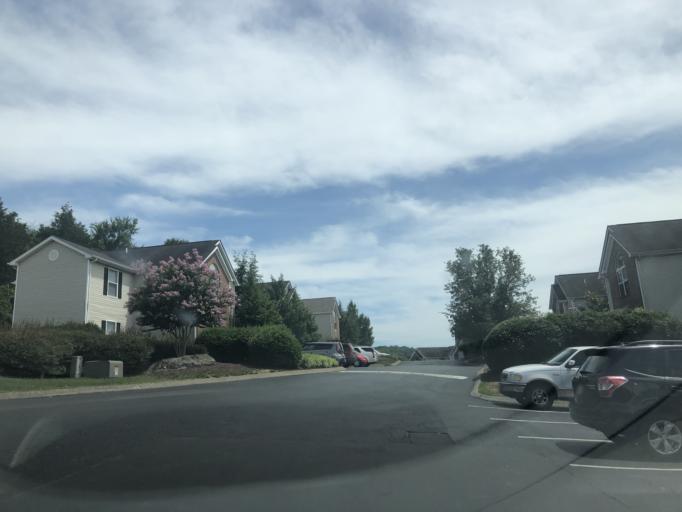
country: US
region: Tennessee
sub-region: Davidson County
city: Belle Meade
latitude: 36.0757
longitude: -86.9288
